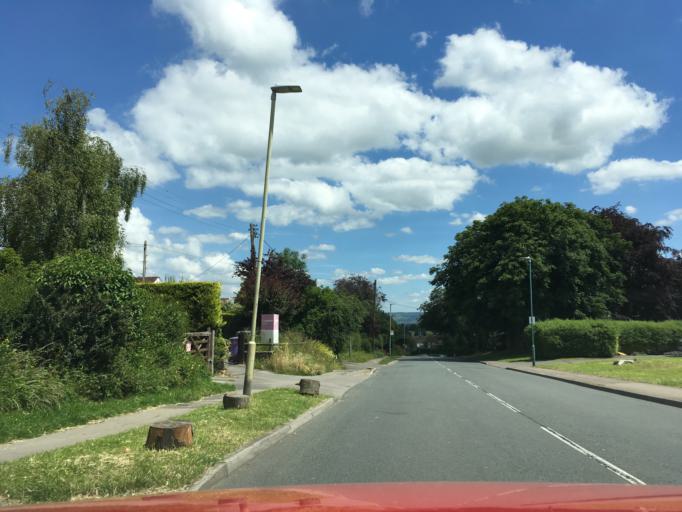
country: GB
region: England
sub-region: Gloucestershire
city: Dursley
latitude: 51.6959
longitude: -2.3709
